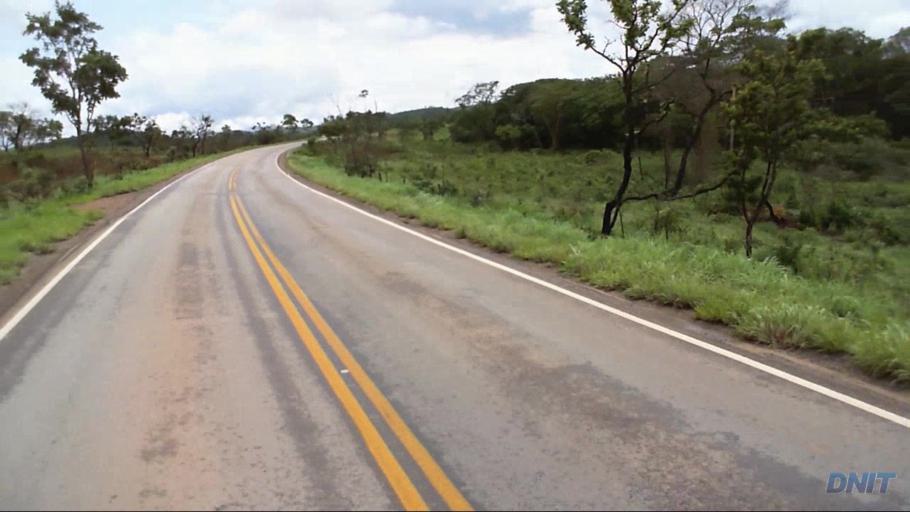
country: BR
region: Goias
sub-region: Padre Bernardo
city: Padre Bernardo
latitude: -15.4649
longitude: -48.2248
